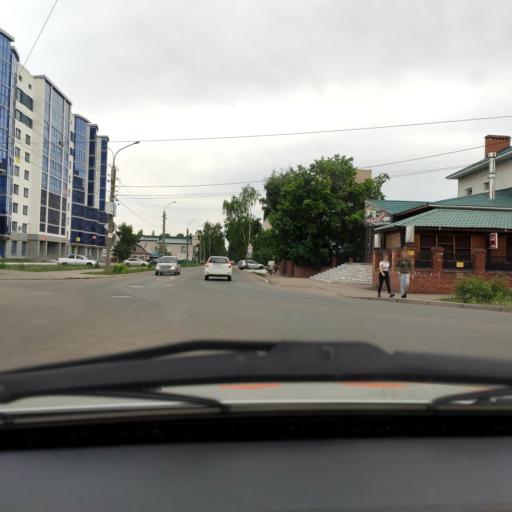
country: RU
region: Bashkortostan
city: Sterlitamak
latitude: 53.6229
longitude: 55.9593
